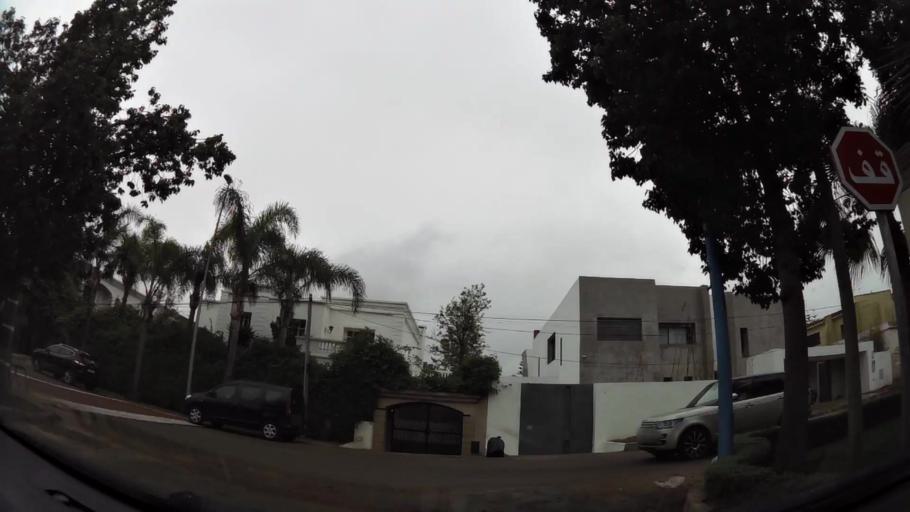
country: MA
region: Grand Casablanca
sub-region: Casablanca
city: Casablanca
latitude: 33.5399
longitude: -7.6273
